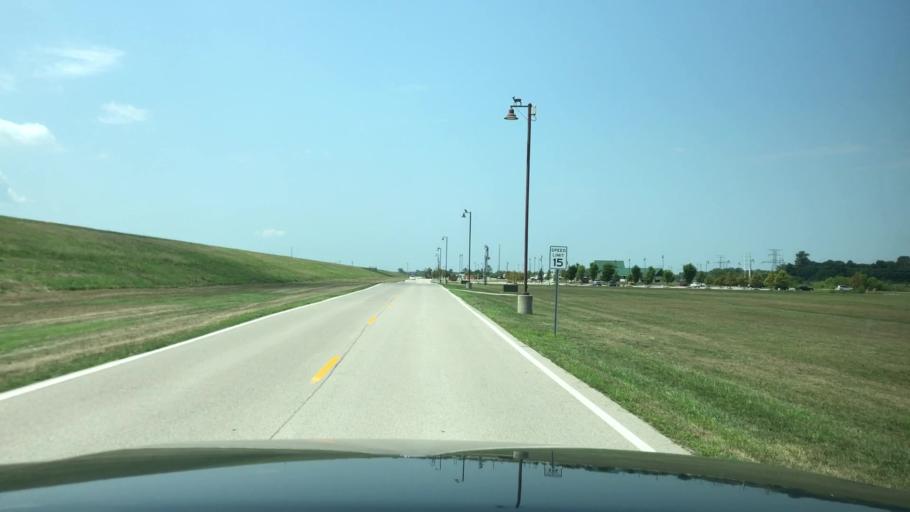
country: US
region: Missouri
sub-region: Saint Charles County
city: Saint Peters
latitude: 38.8215
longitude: -90.5653
